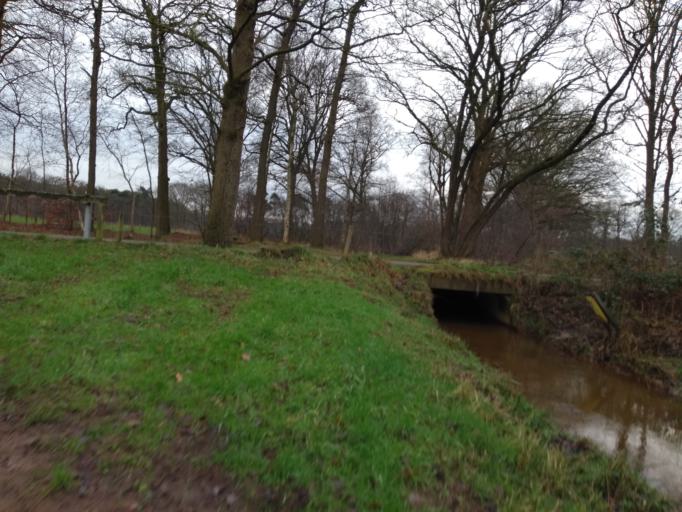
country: NL
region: Overijssel
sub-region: Gemeente Hengelo
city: Hengelo
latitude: 52.2253
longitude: 6.7990
